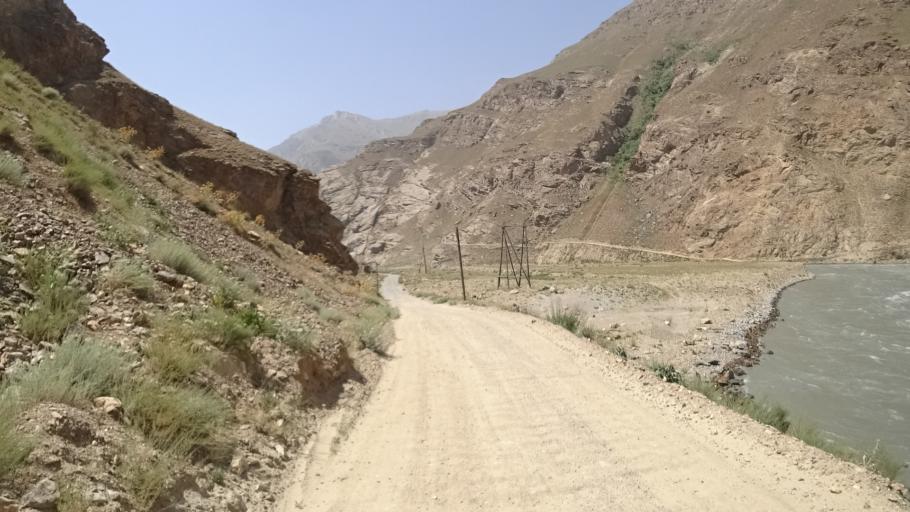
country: TJ
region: Gorno-Badakhshan
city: Khorugh
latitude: 37.1443
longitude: 71.4482
